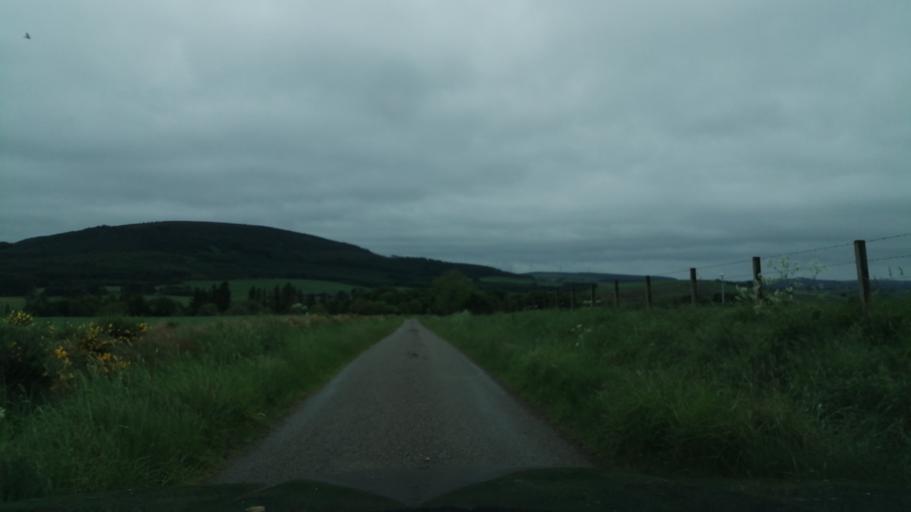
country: GB
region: Scotland
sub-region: Moray
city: Keith
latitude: 57.5555
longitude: -2.8680
